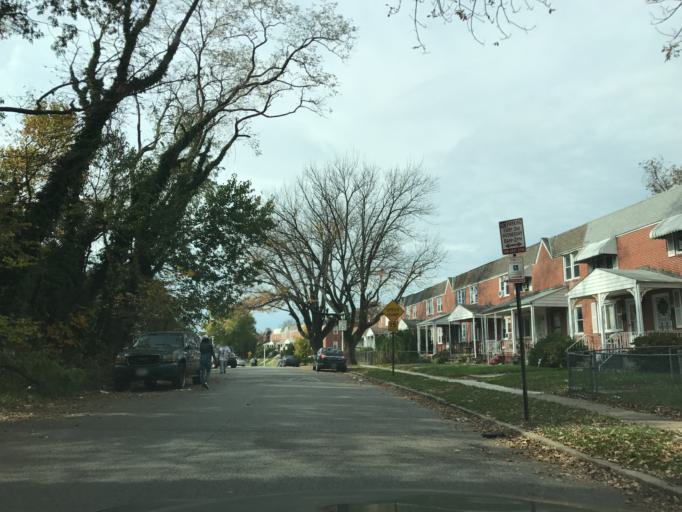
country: US
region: Maryland
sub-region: Baltimore County
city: Lochearn
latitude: 39.3424
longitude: -76.6619
